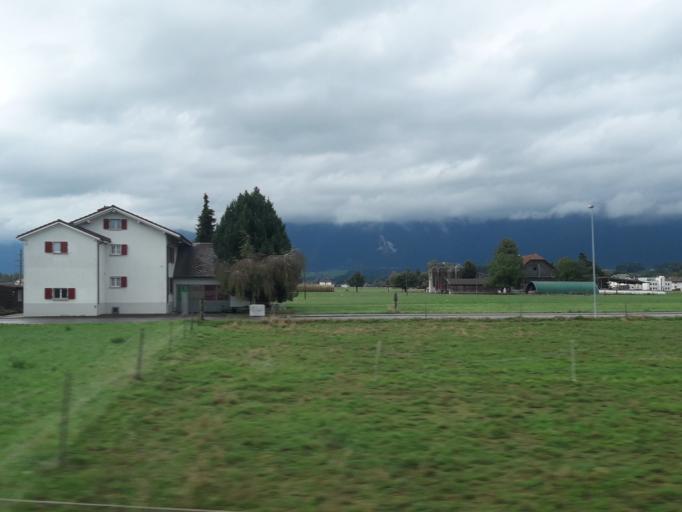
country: CH
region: Bern
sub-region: Thun District
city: Uetendorf
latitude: 46.7736
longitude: 7.5866
